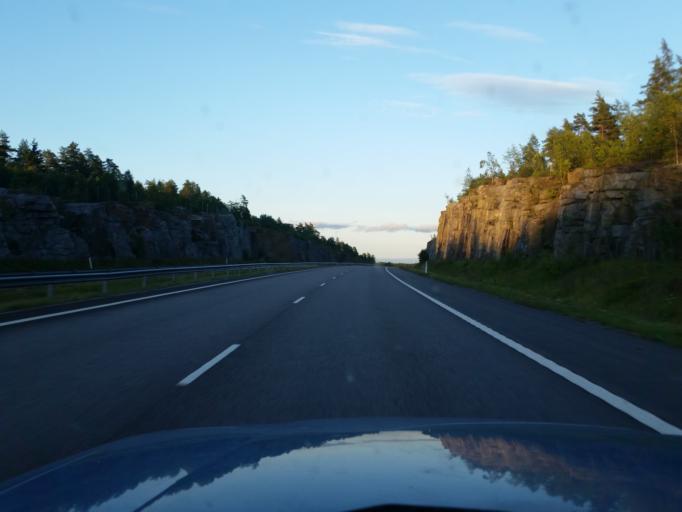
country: FI
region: Varsinais-Suomi
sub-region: Salo
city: Halikko
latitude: 60.4357
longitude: 22.9582
